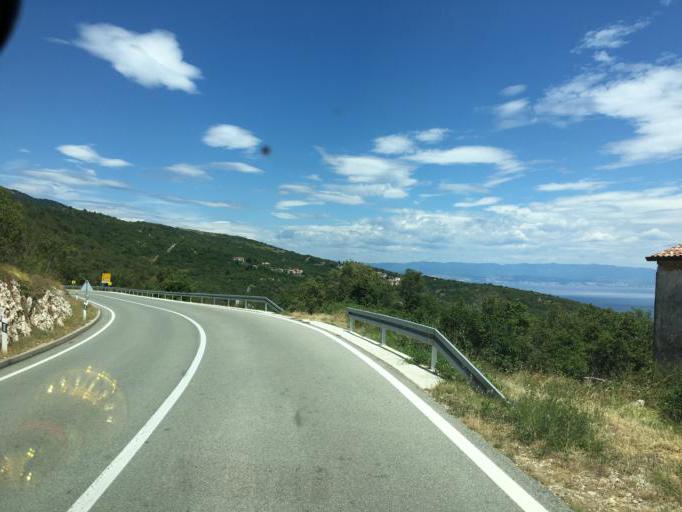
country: HR
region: Istarska
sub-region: Grad Labin
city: Rabac
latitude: 45.1514
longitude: 14.2142
